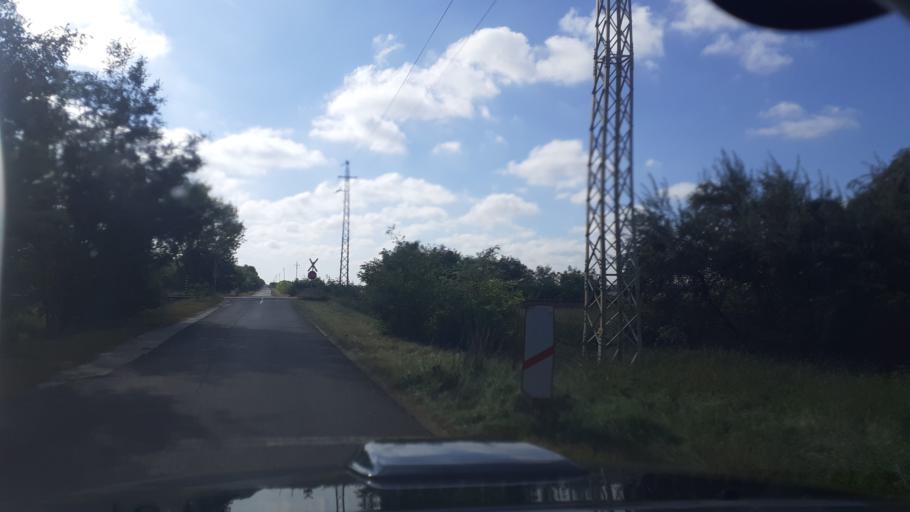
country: HU
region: Fejer
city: Baracs
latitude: 46.9372
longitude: 18.8679
